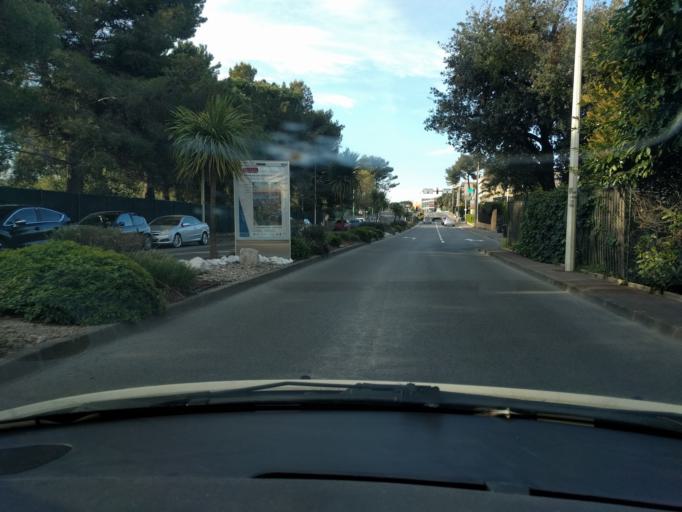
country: FR
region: Provence-Alpes-Cote d'Azur
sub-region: Departement des Alpes-Maritimes
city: Cannes
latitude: 43.5703
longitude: 6.9821
